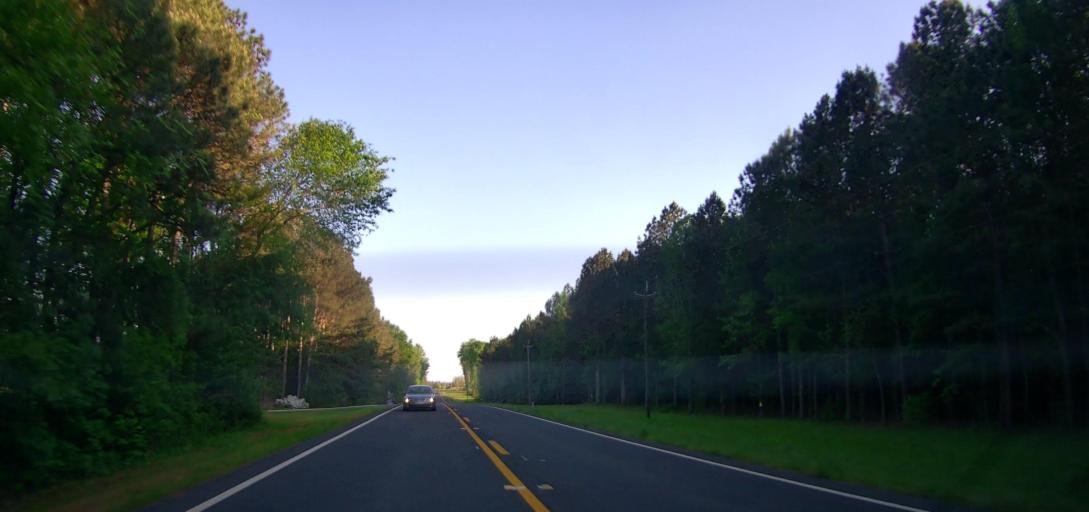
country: US
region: Georgia
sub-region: Jasper County
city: Monticello
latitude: 33.4805
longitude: -83.6452
